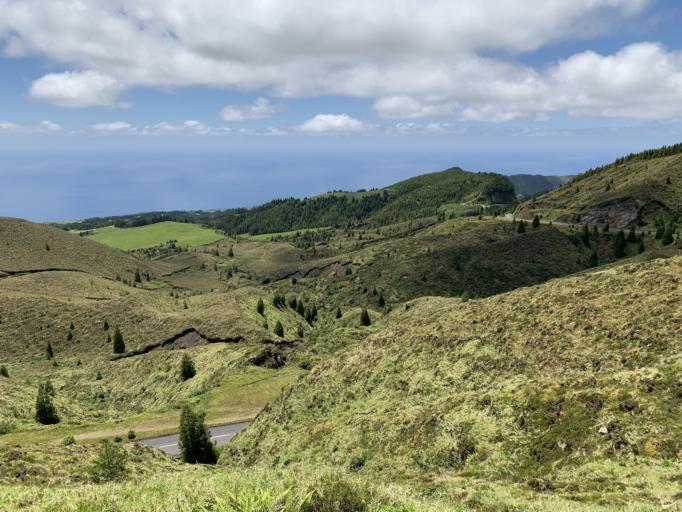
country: PT
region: Azores
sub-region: Ponta Delgada
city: Arrifes
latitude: 37.8372
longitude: -25.7631
